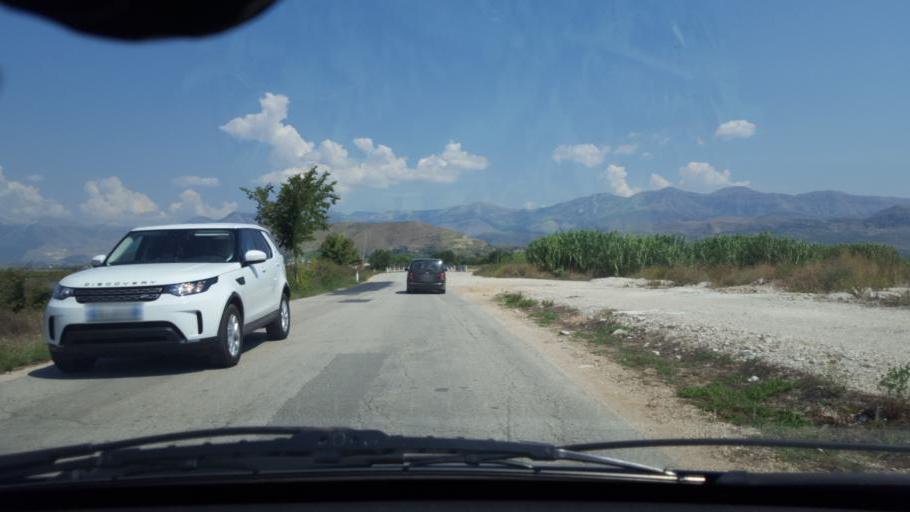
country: AL
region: Vlore
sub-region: Rrethi i Delvines
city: Finiq
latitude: 39.8827
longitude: 20.0562
